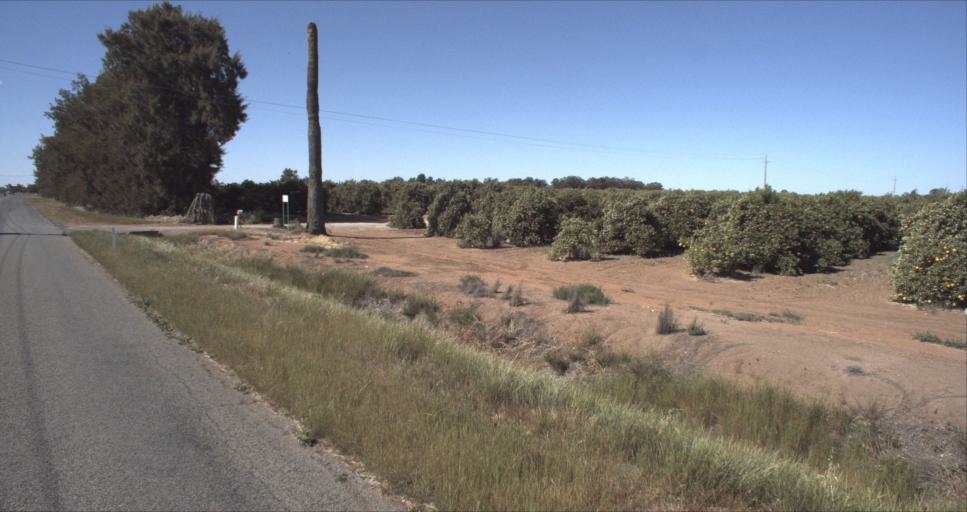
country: AU
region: New South Wales
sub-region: Leeton
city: Leeton
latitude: -34.5672
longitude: 146.3824
